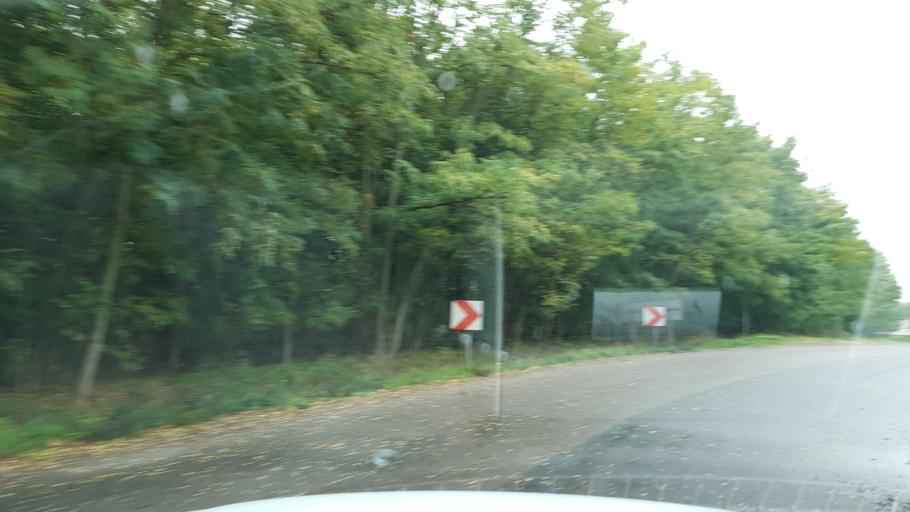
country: PL
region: West Pomeranian Voivodeship
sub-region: Powiat mysliborski
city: Mysliborz
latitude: 52.9947
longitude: 14.8602
